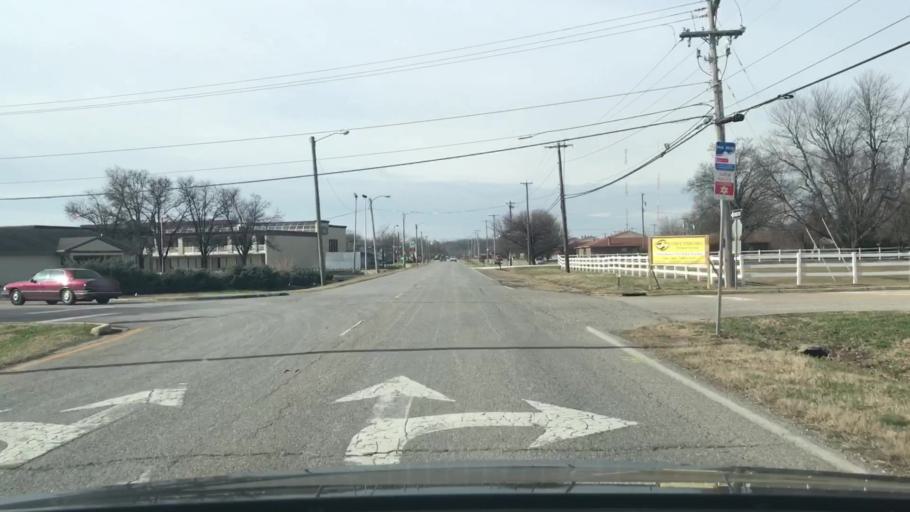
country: US
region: Kentucky
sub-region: Daviess County
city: Owensboro
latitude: 37.7739
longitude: -87.1480
